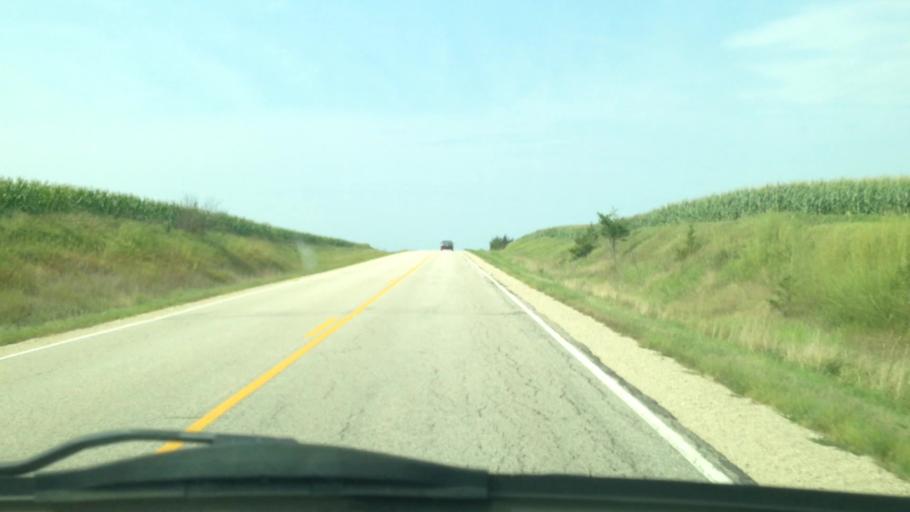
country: US
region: Minnesota
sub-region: Winona County
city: Saint Charles
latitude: 43.8765
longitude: -91.9594
